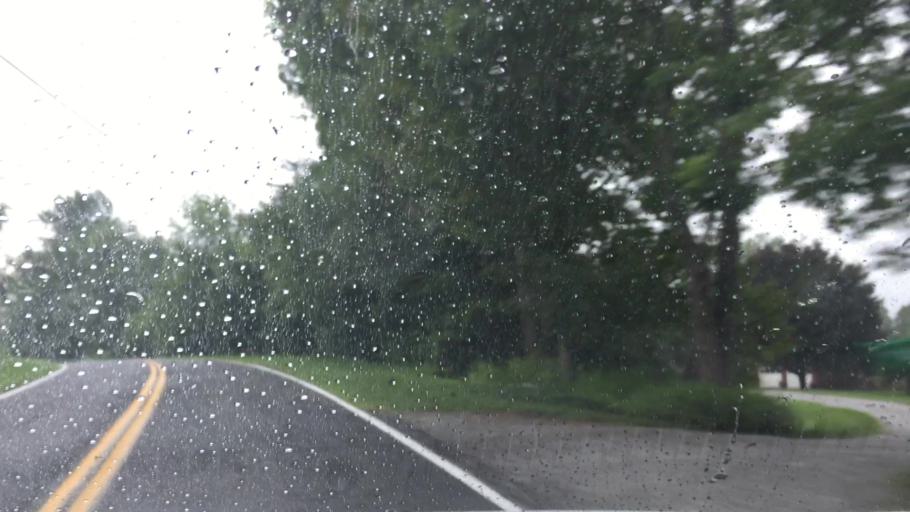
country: US
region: Massachusetts
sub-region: Berkshire County
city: Housatonic
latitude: 42.2952
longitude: -73.4033
